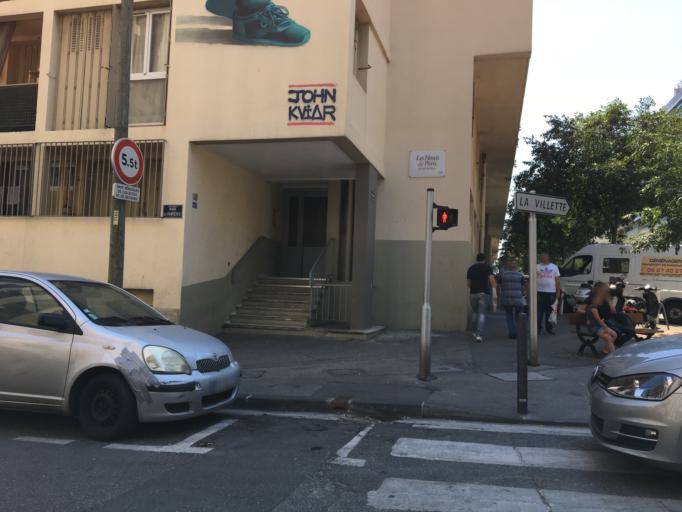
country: FR
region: Provence-Alpes-Cote d'Azur
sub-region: Departement des Bouches-du-Rhone
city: Marseille 03
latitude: 43.3075
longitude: 5.3715
